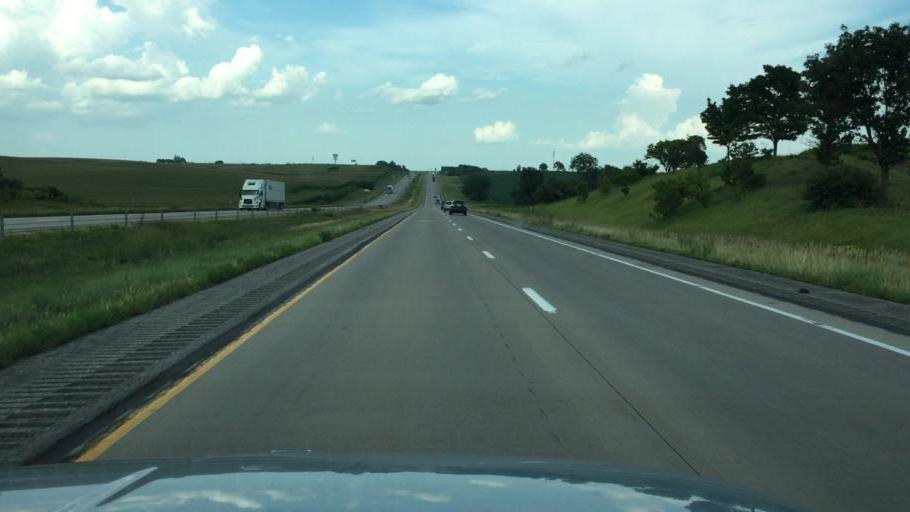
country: US
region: Iowa
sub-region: Iowa County
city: Williamsburg
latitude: 41.6907
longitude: -92.0884
